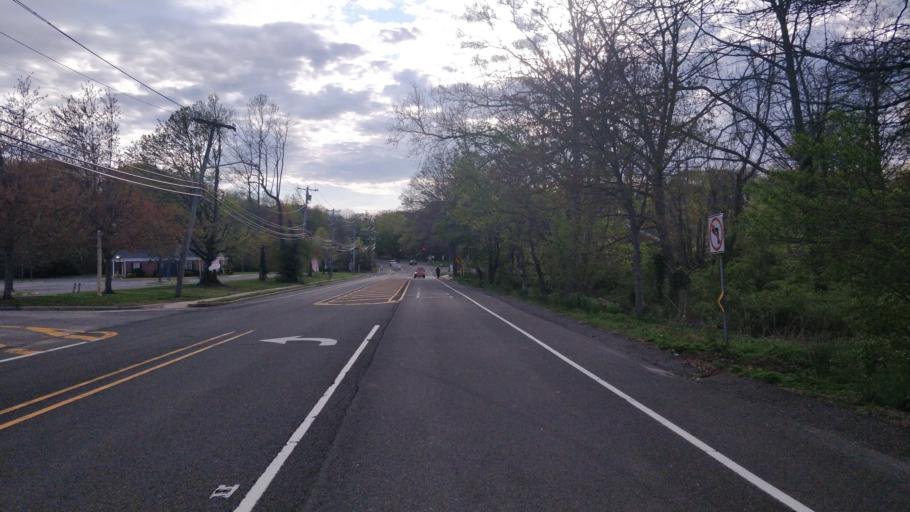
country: US
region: New York
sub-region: Suffolk County
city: Fort Salonga
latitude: 40.9125
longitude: -73.2987
